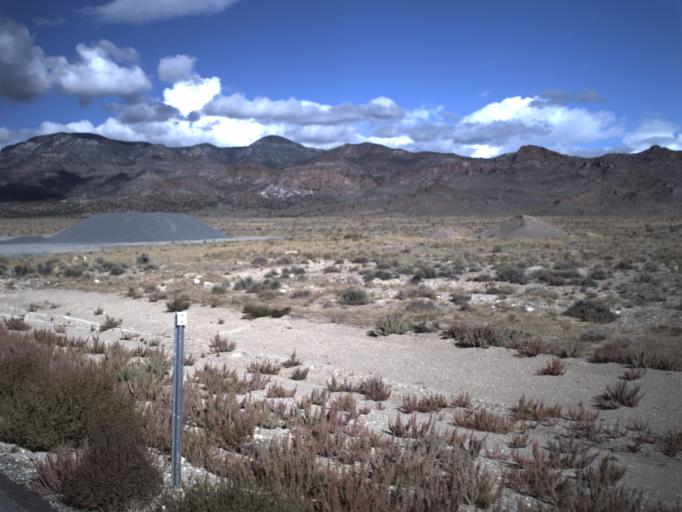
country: US
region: Utah
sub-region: Beaver County
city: Milford
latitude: 38.4928
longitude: -113.4755
